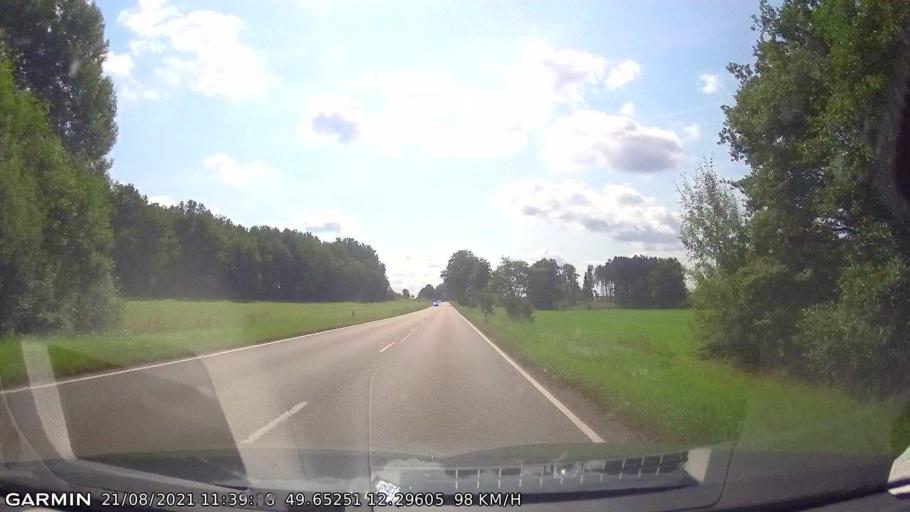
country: DE
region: Bavaria
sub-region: Upper Palatinate
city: Waldthurn
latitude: 49.6525
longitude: 12.2960
